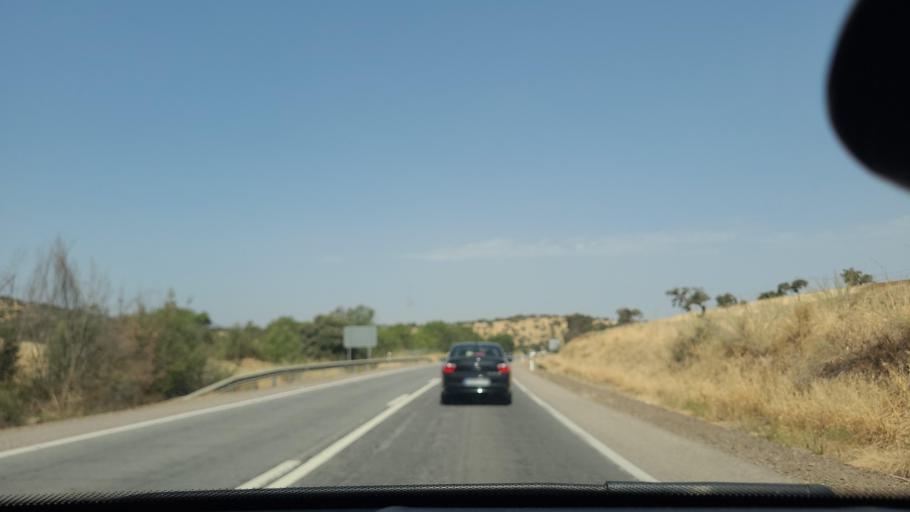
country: ES
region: Extremadura
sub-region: Provincia de Badajoz
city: Zafra
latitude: 38.4599
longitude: -6.4380
